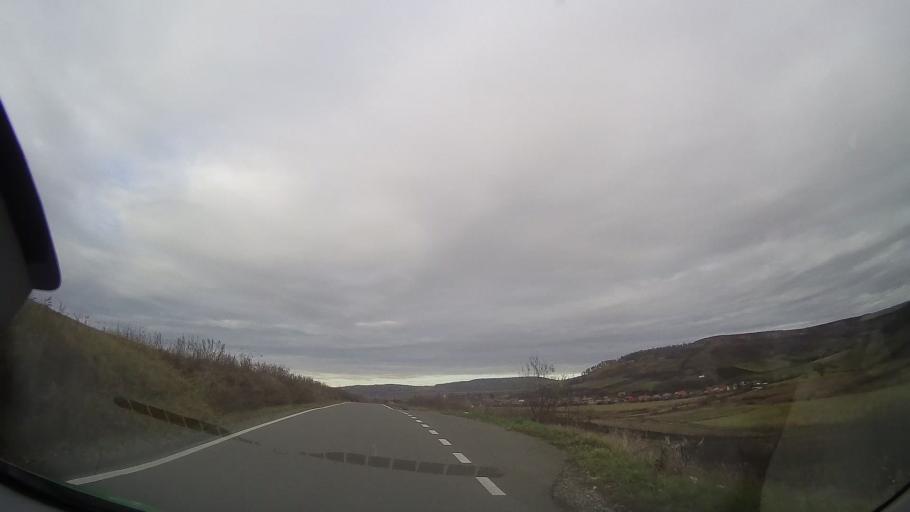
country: RO
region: Mures
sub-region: Comuna Faragau
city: Faragau
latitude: 46.7705
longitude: 24.5571
